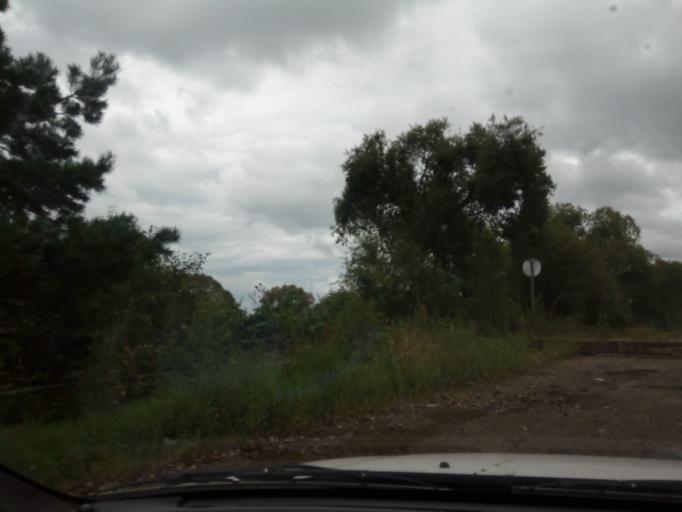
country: RU
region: Primorskiy
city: Dal'nerechensk
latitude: 45.9162
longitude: 133.7247
